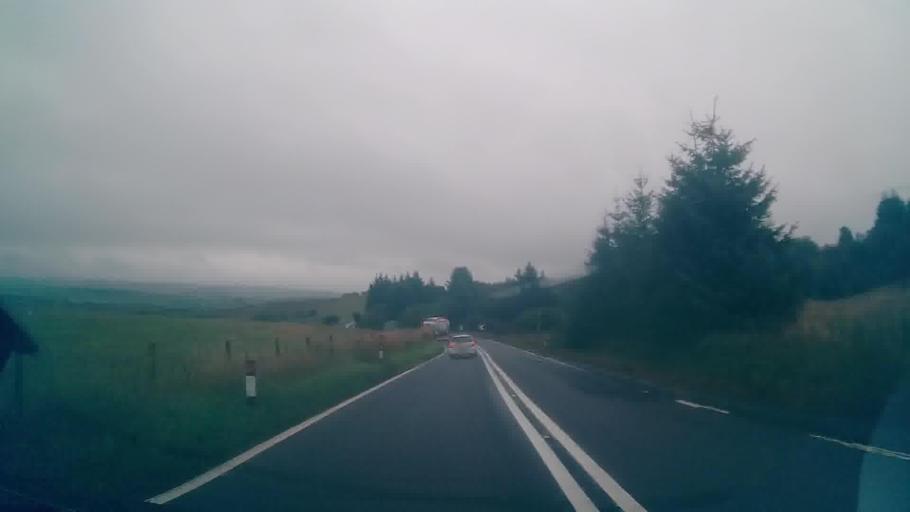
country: GB
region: Scotland
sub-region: Dumfries and Galloway
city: Kirkconnel
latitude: 55.3884
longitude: -4.0547
